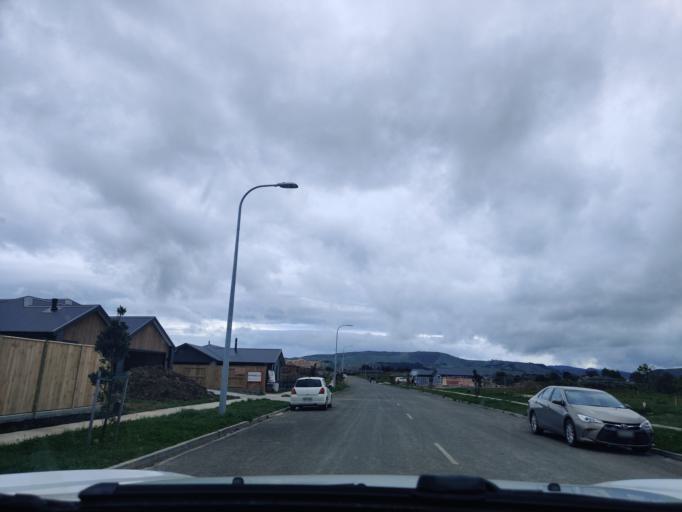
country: NZ
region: Manawatu-Wanganui
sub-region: Palmerston North City
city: Palmerston North
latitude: -40.3878
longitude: 175.6472
